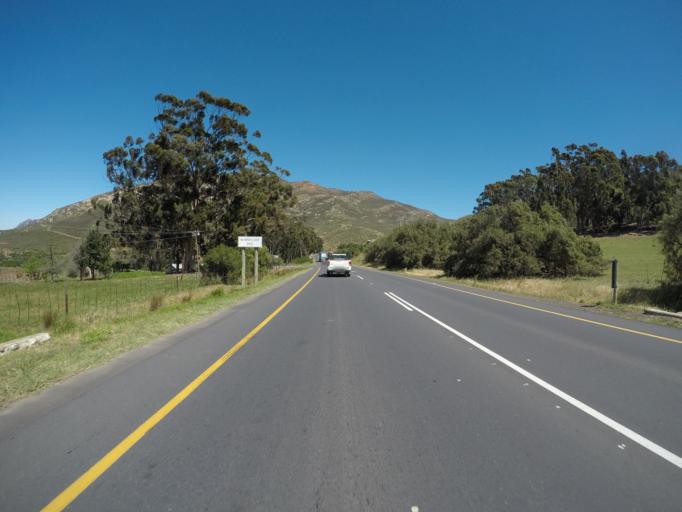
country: ZA
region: Western Cape
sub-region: Cape Winelands District Municipality
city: Ceres
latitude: -33.3154
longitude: 19.0928
